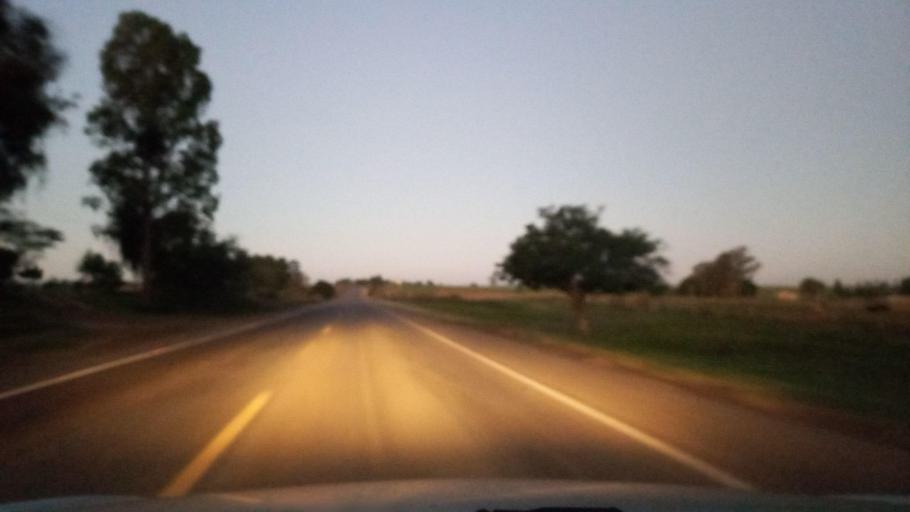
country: BR
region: Rio Grande do Sul
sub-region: Rosario Do Sul
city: Rosario do Sul
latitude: -30.2367
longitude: -54.7814
